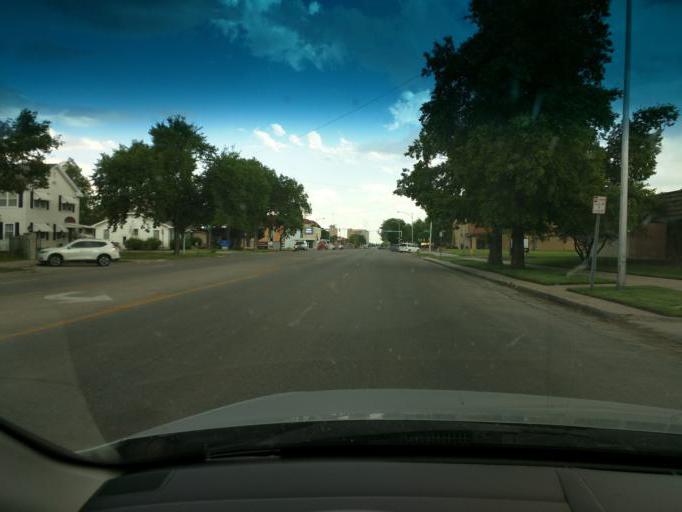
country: US
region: Kansas
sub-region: Reno County
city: Hutchinson
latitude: 38.0645
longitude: -97.9320
